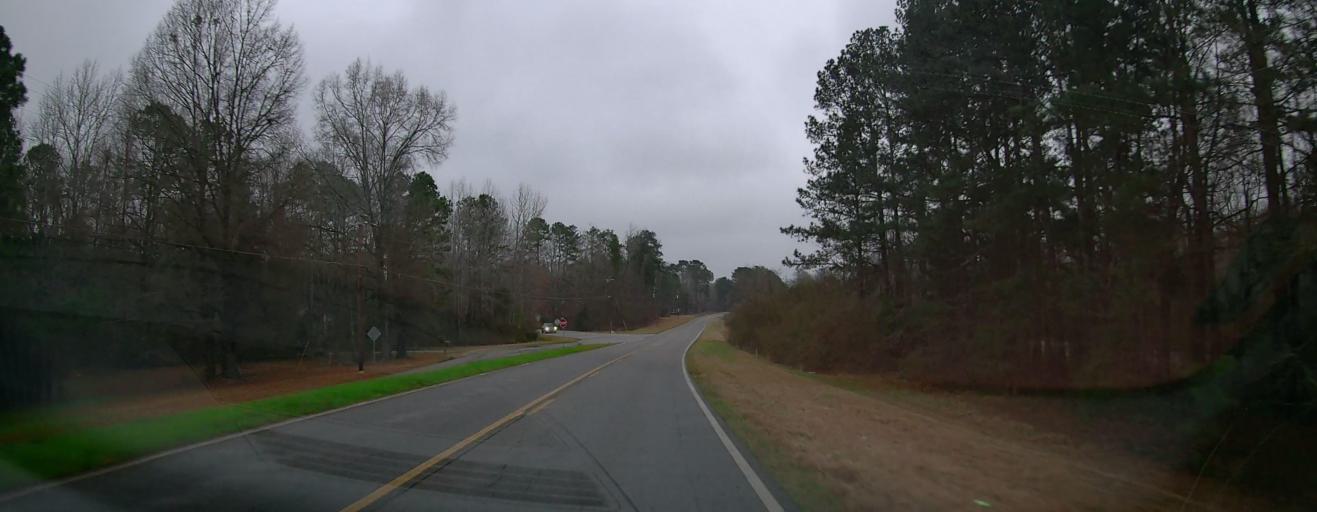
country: US
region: Georgia
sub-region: Spalding County
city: East Griffin
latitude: 33.1478
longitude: -84.1991
